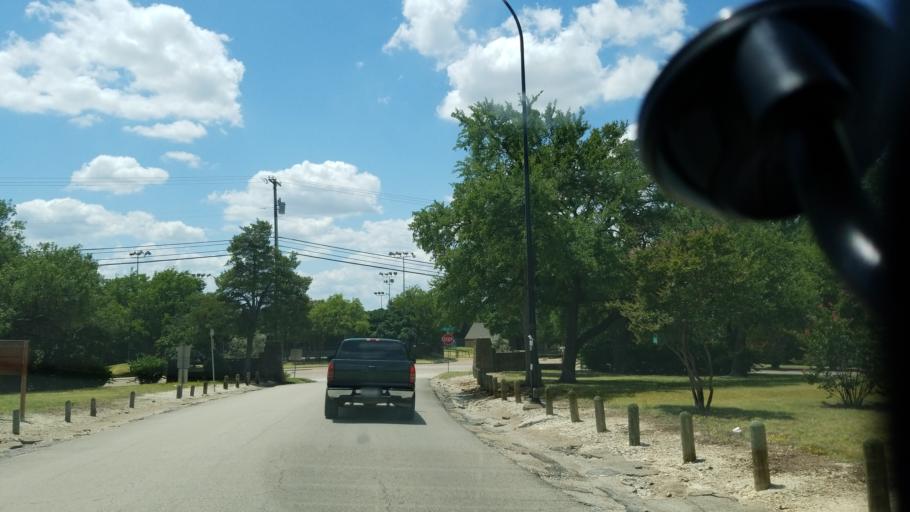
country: US
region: Texas
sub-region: Dallas County
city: Cockrell Hill
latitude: 32.7063
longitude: -96.8544
